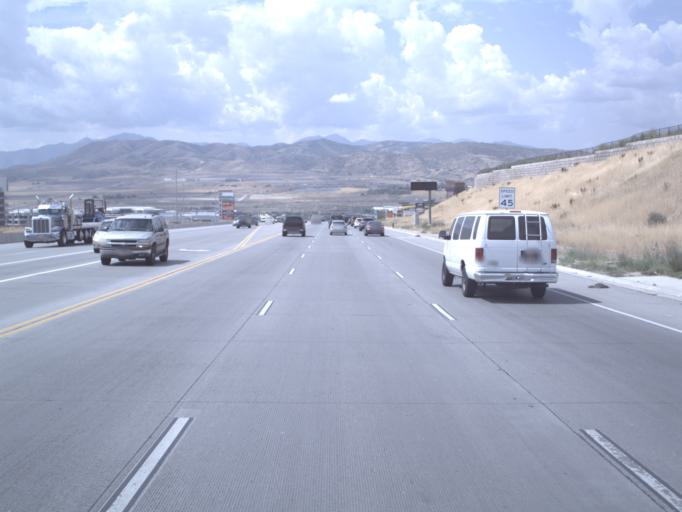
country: US
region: Utah
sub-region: Utah County
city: Lehi
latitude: 40.4318
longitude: -111.8814
